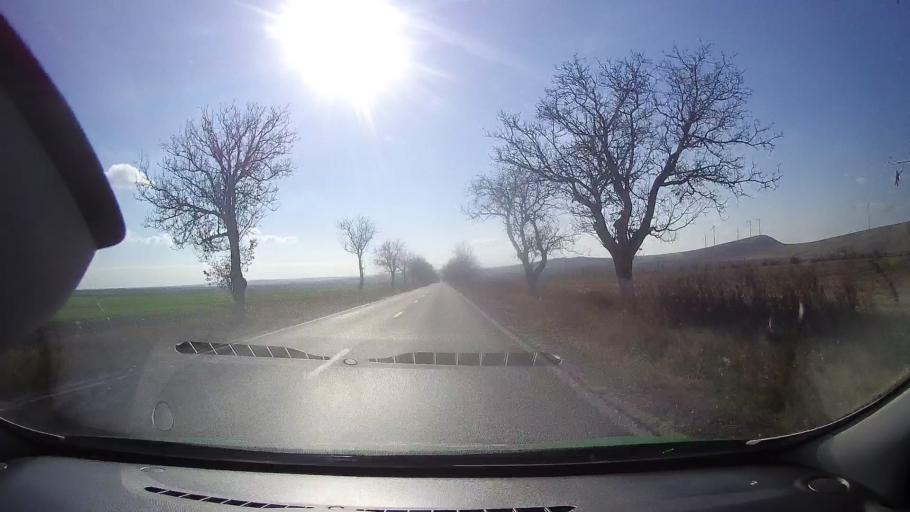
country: RO
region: Tulcea
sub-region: Comuna Ceamurlia de Jos
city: Ceamurlia de Jos
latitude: 44.7862
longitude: 28.6895
